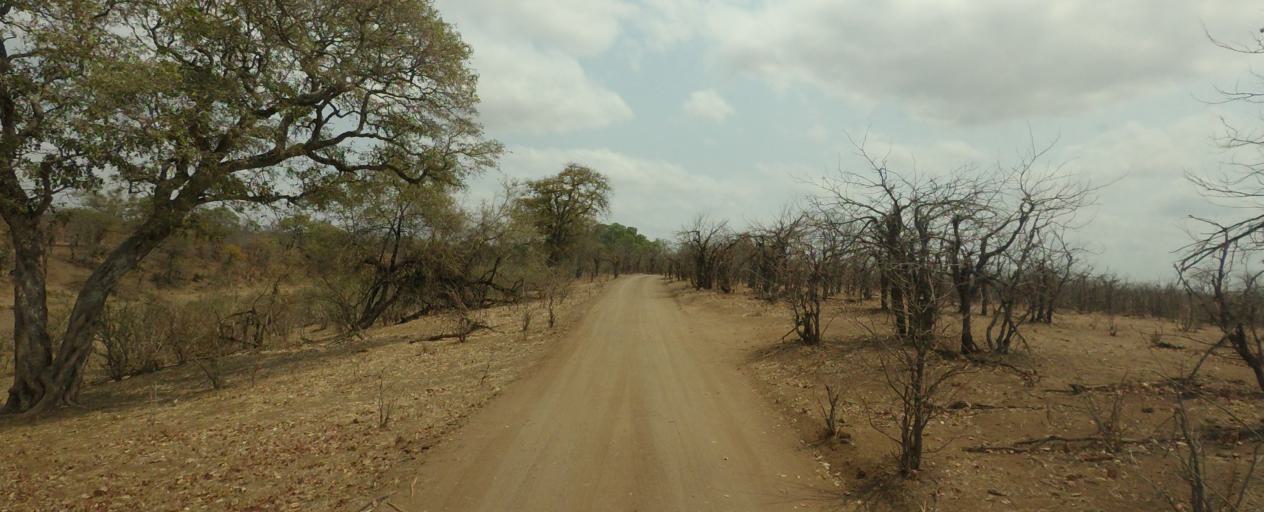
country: ZA
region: Limpopo
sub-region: Mopani District Municipality
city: Phalaborwa
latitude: -23.5414
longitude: 31.4246
